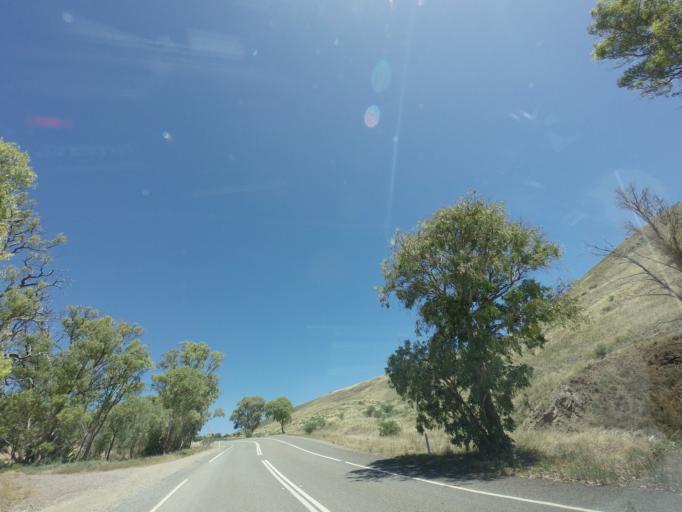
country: AU
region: South Australia
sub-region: Flinders Ranges
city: Quorn
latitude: -32.6382
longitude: 138.0354
